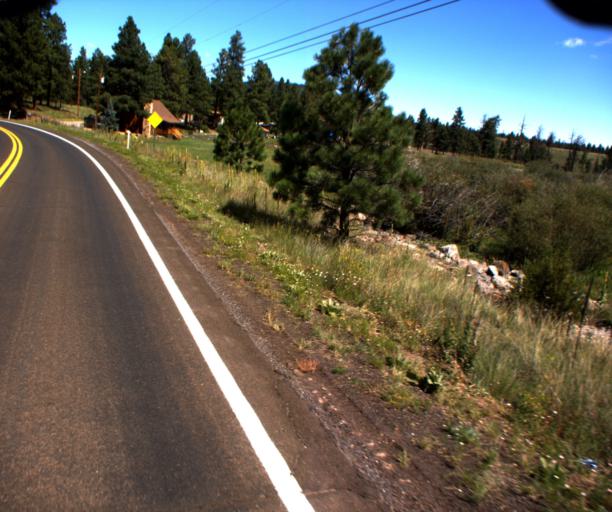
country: US
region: Arizona
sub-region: Apache County
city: Eagar
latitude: 34.0591
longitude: -109.4617
